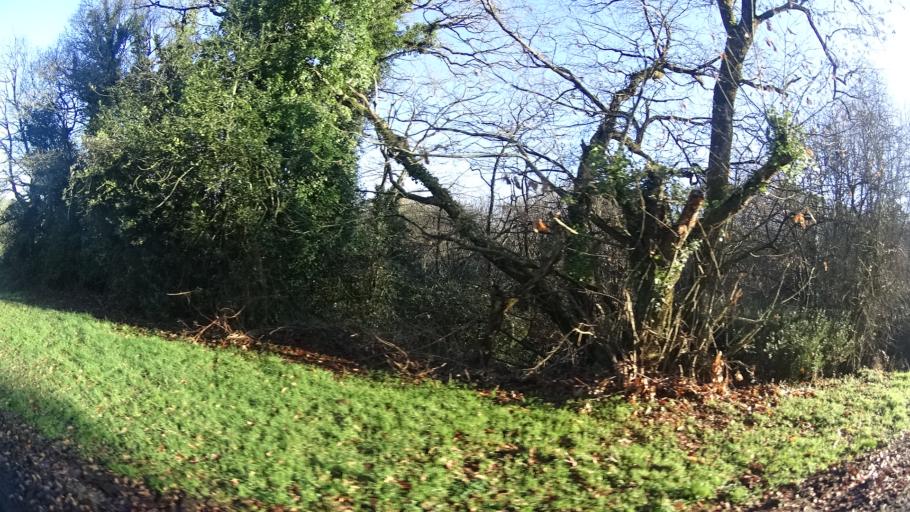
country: FR
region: Brittany
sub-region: Departement du Morbihan
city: Saint-Jacut-les-Pins
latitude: 47.6630
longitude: -2.2101
